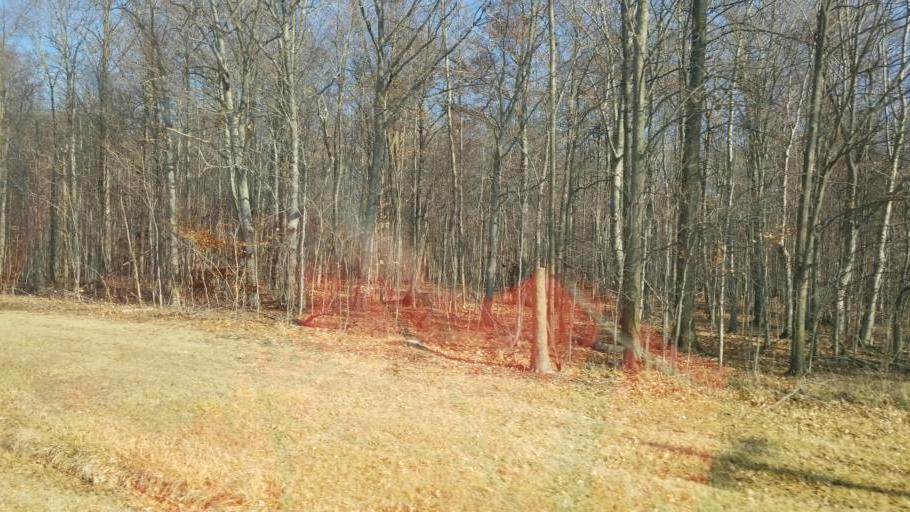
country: US
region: Ohio
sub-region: Seneca County
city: Tiffin
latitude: 40.9979
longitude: -83.0742
